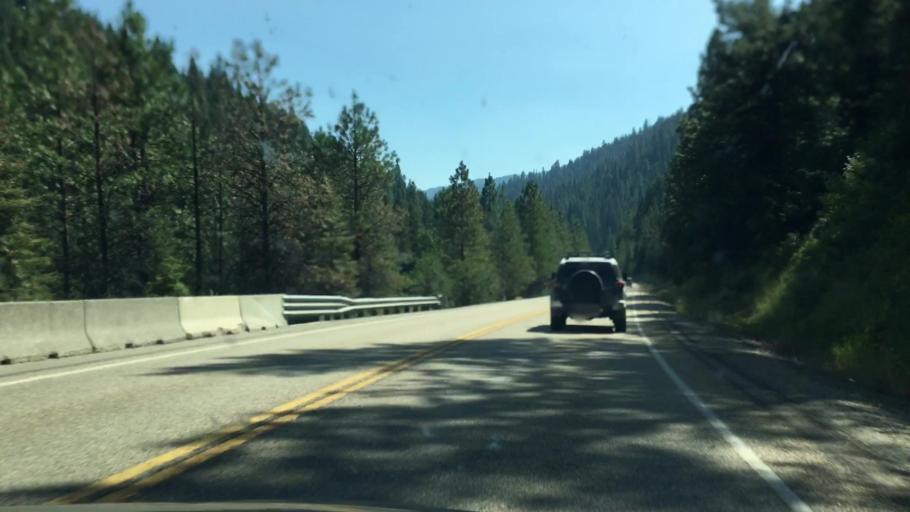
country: US
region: Idaho
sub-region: Valley County
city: Cascade
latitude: 44.2035
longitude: -116.1096
